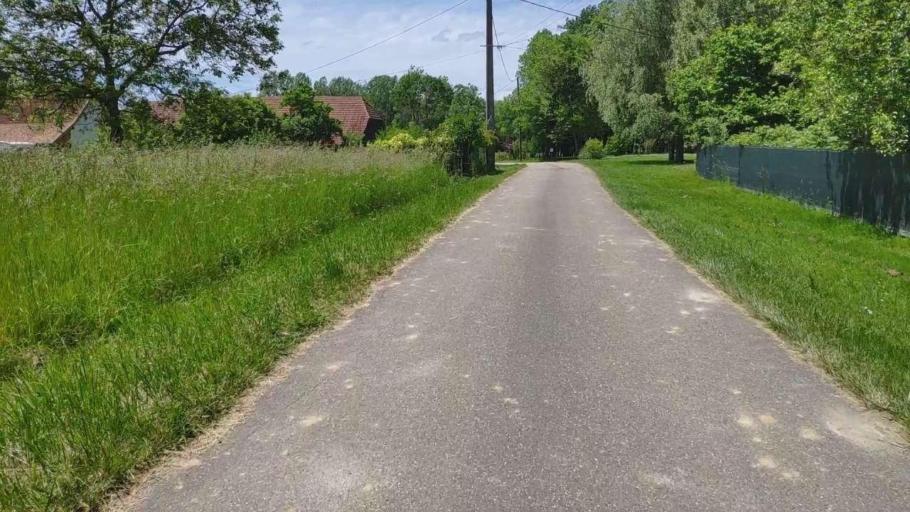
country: FR
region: Franche-Comte
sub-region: Departement du Jura
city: Bletterans
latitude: 46.7830
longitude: 5.3793
